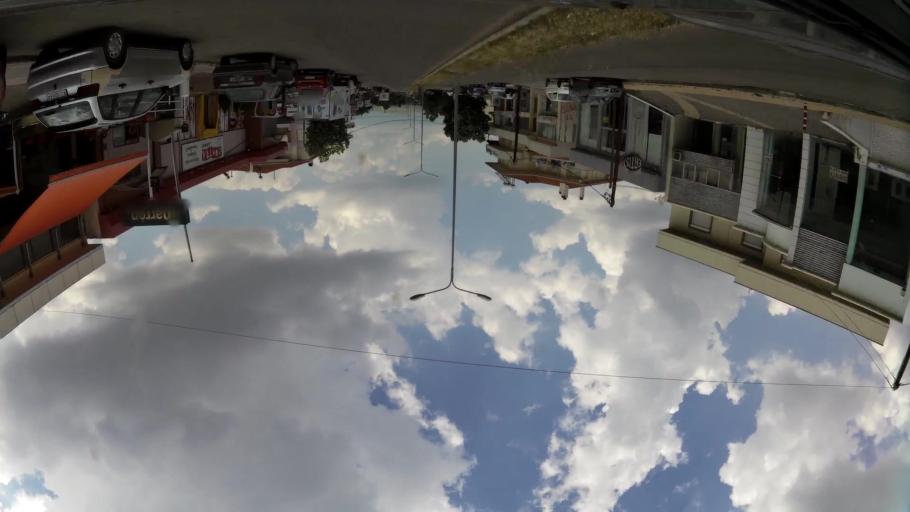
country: GR
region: West Macedonia
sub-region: Nomos Kozanis
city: Kozani
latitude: 40.2997
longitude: 21.8014
